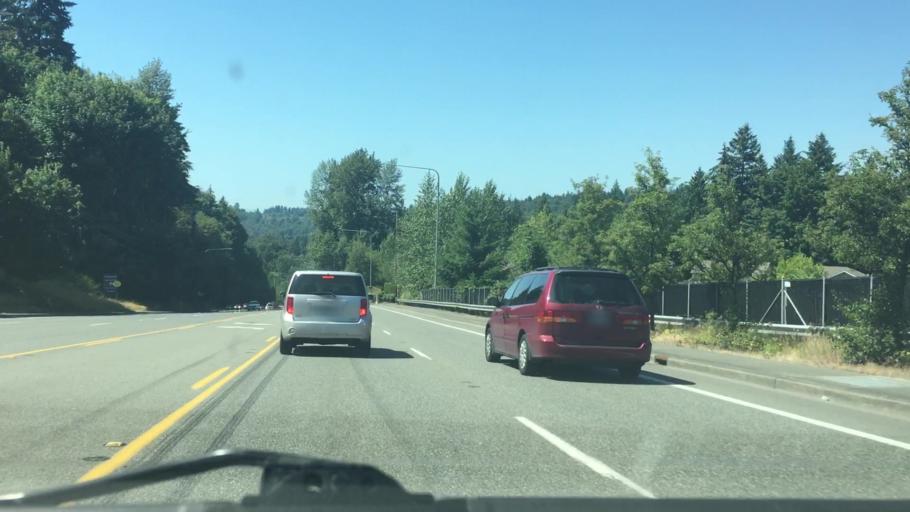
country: US
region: Washington
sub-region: King County
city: Fairwood
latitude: 47.4641
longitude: -122.1517
